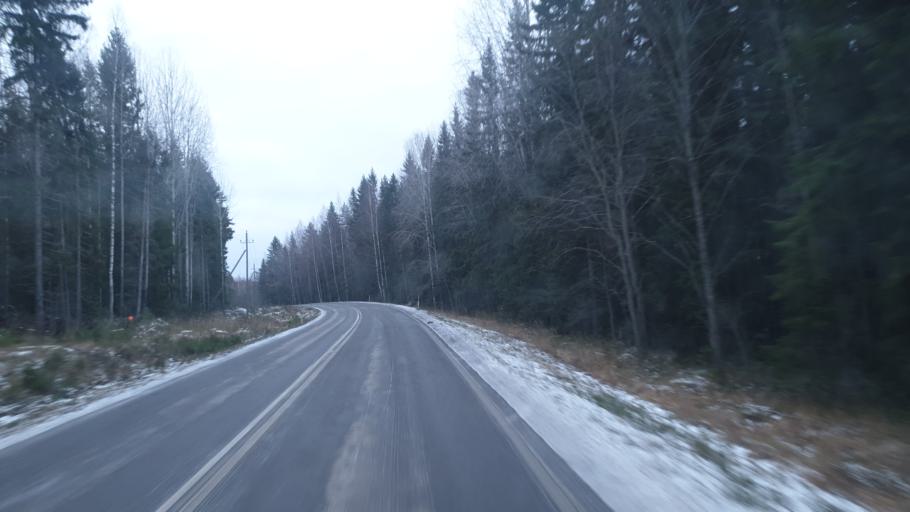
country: FI
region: Southern Savonia
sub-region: Pieksaemaeki
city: Joroinen
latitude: 62.2046
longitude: 27.9676
